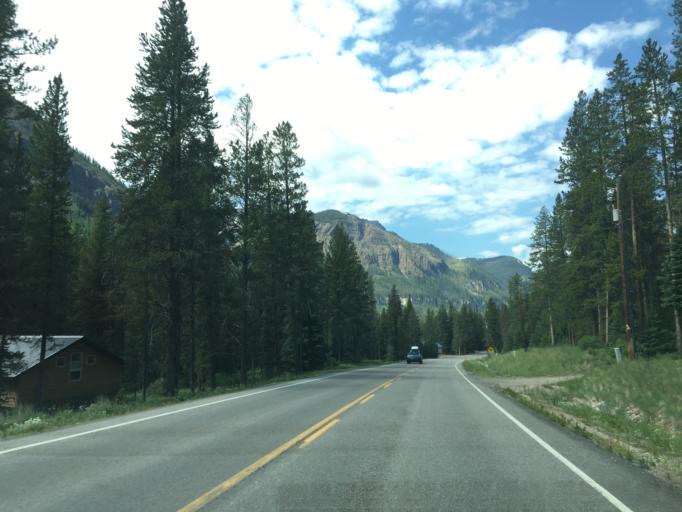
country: US
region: Montana
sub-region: Stillwater County
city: Absarokee
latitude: 45.0104
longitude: -109.9767
